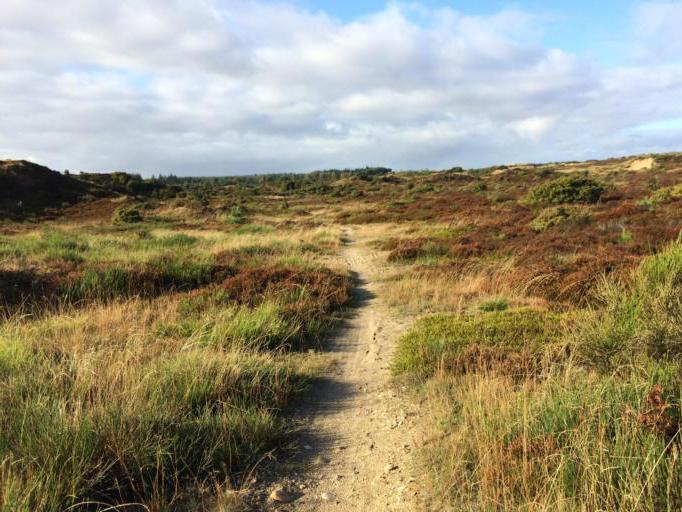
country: DK
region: Central Jutland
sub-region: Holstebro Kommune
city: Ulfborg
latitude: 56.2534
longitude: 8.4157
